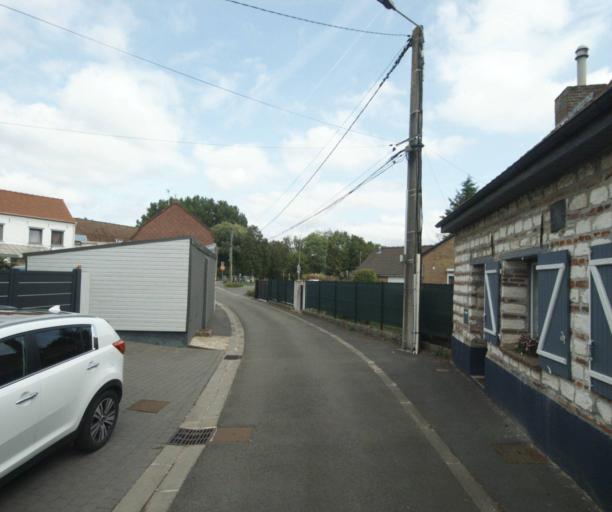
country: FR
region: Nord-Pas-de-Calais
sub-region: Departement du Nord
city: Tressin
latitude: 50.6113
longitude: 3.1936
